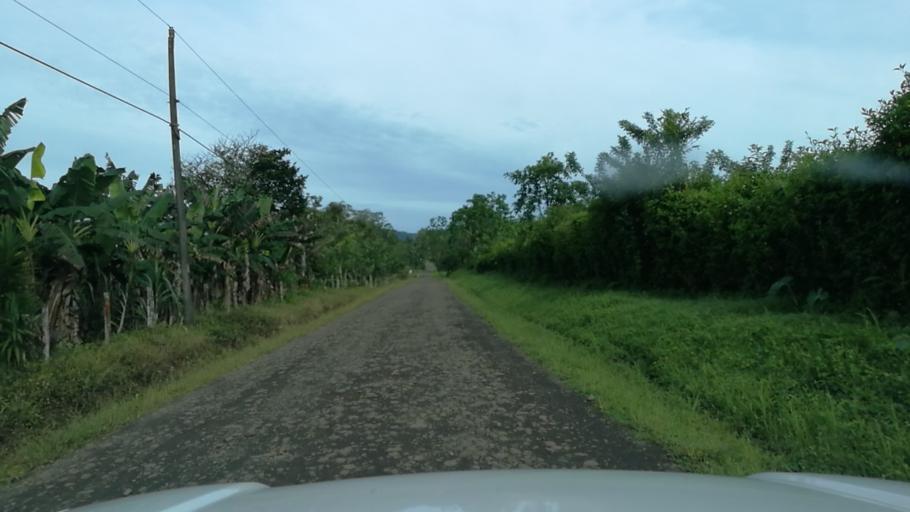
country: CR
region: Alajuela
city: Bijagua
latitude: 10.7127
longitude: -84.9165
